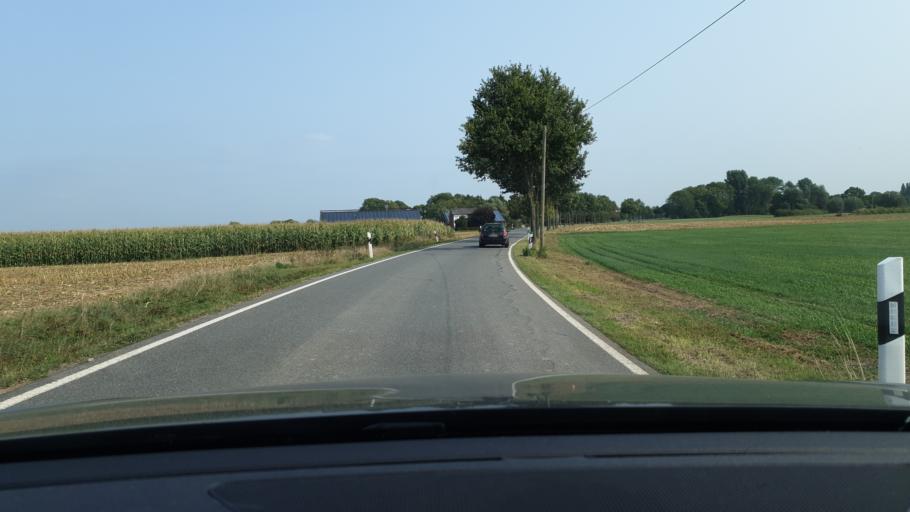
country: DE
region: North Rhine-Westphalia
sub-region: Regierungsbezirk Dusseldorf
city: Kranenburg
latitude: 51.8484
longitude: 6.0533
